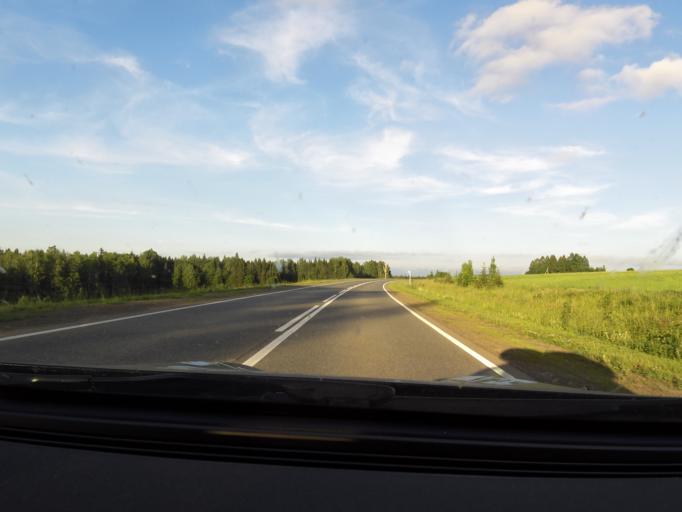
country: RU
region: Perm
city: Siva
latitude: 58.5409
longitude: 53.9528
